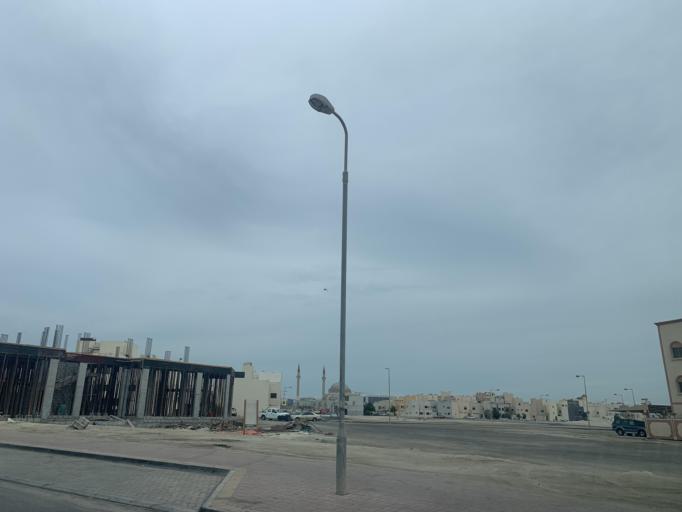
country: BH
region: Muharraq
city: Al Hadd
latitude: 26.2714
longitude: 50.6562
